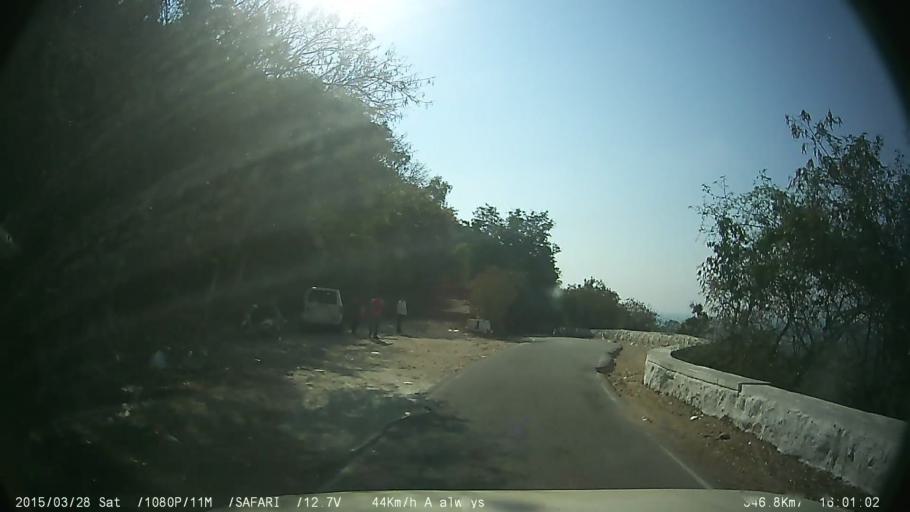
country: IN
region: Karnataka
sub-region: Mysore
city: Mysore
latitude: 12.2798
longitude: 76.6736
